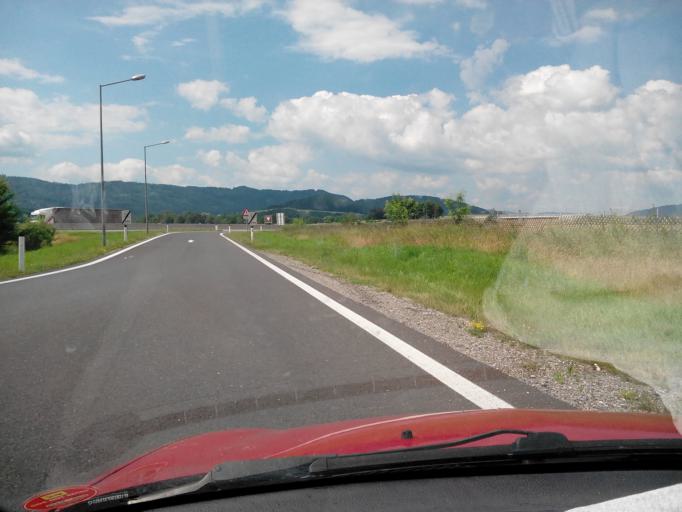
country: AT
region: Upper Austria
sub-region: Politischer Bezirk Vocklabruck
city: Aurach am Hongar
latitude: 47.9564
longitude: 13.6394
